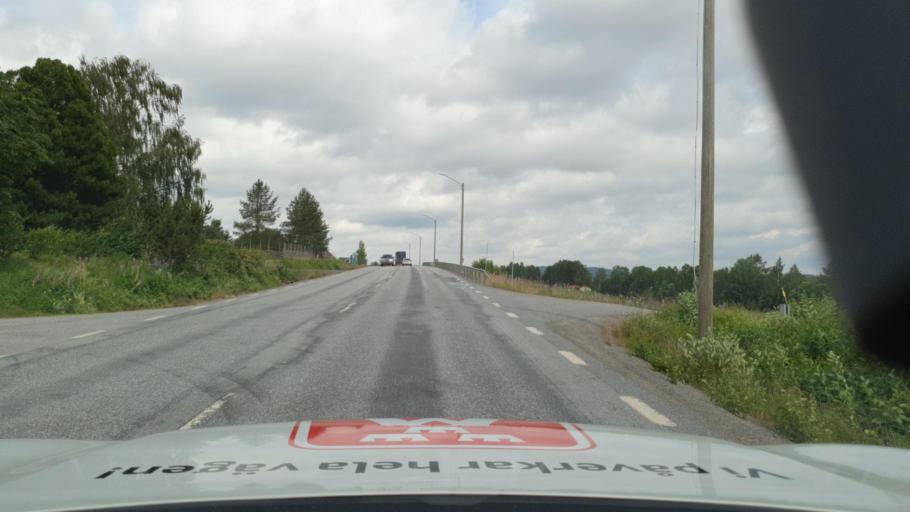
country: SE
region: Vaesterbotten
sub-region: Vannas Kommun
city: Vannasby
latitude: 64.0144
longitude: 20.0322
